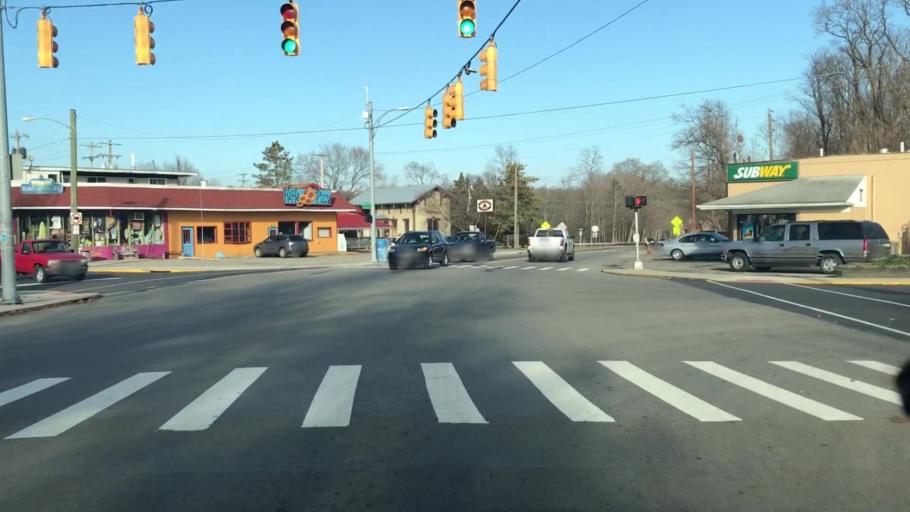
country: US
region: Ohio
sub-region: Greene County
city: Yellow Springs
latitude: 39.8063
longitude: -83.8884
